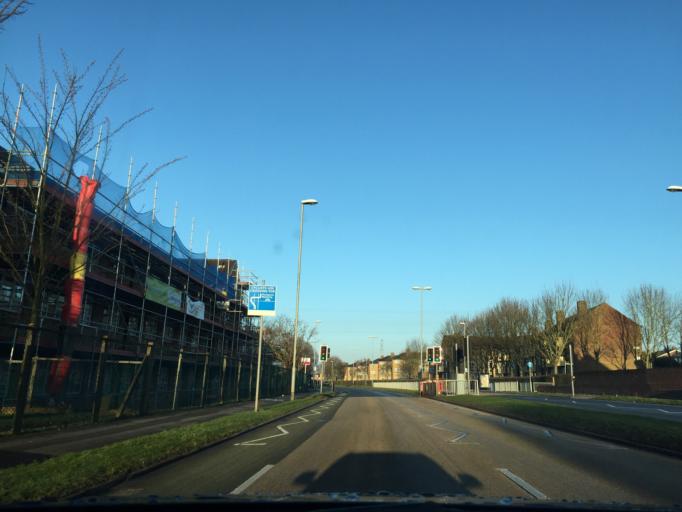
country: GB
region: England
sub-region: Portsmouth
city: Cosham
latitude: 50.8478
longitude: -1.0765
